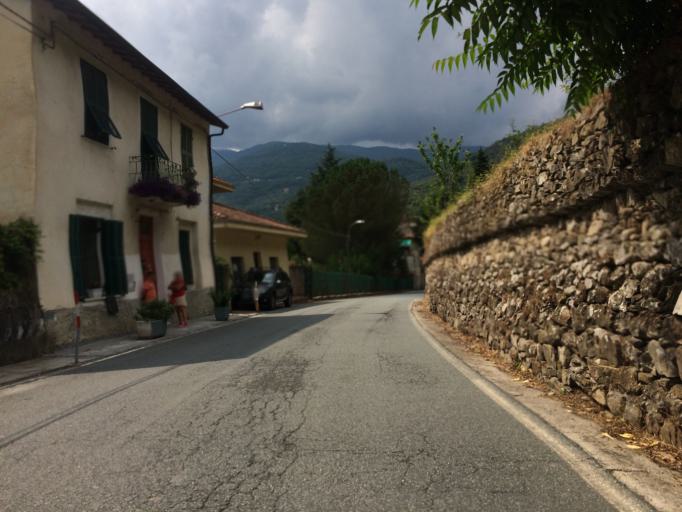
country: IT
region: Liguria
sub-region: Provincia di Imperia
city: Castel Vittorio
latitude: 43.9311
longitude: 7.6687
